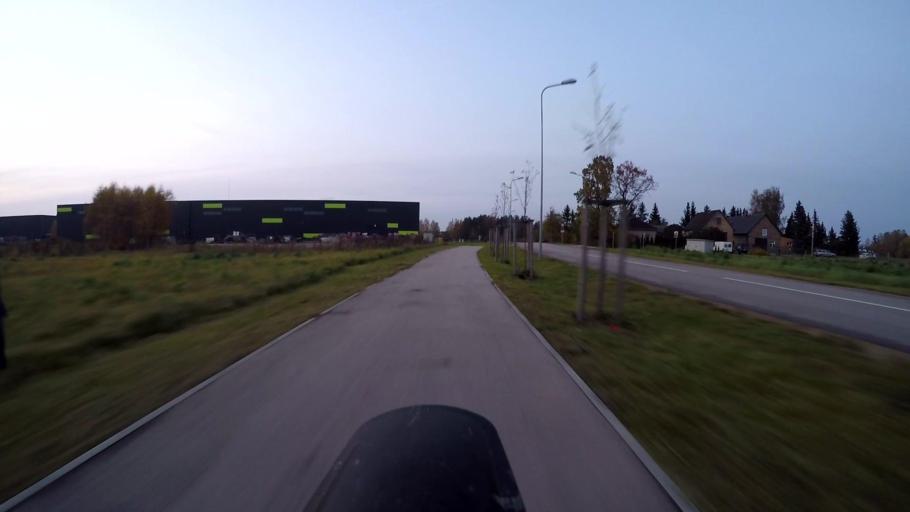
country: LV
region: Marupe
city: Marupe
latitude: 56.9160
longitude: 23.9923
